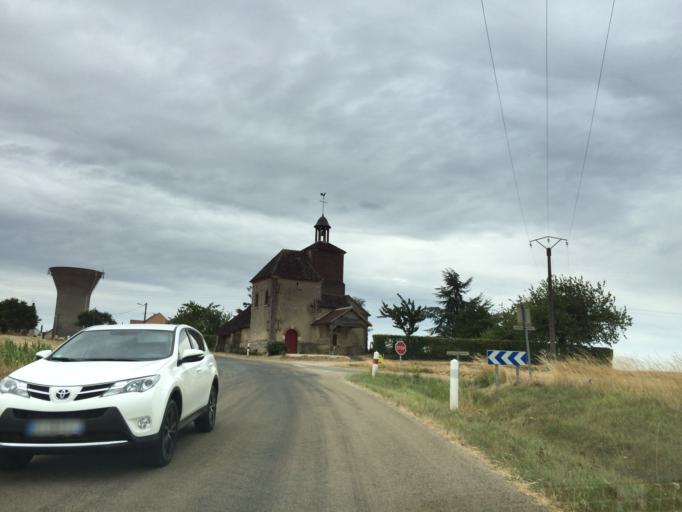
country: FR
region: Bourgogne
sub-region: Departement de l'Yonne
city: Aillant-sur-Tholon
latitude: 47.8706
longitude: 3.3366
